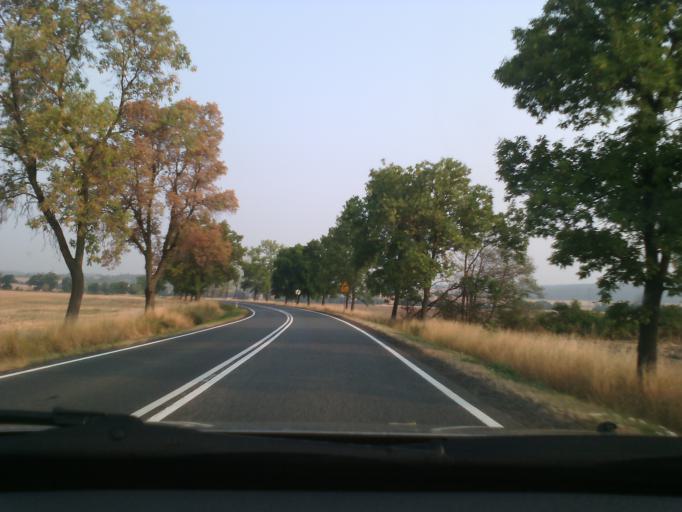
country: PL
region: Lower Silesian Voivodeship
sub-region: Powiat jaworski
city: Bolkow
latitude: 50.9105
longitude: 16.1378
